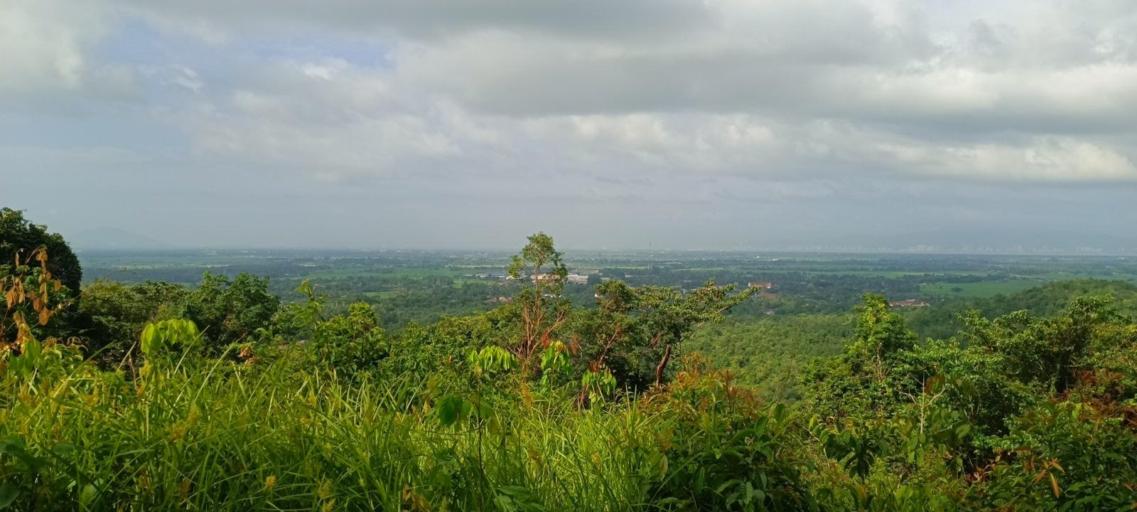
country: MY
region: Kedah
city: Sungai Petani
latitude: 5.6016
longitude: 100.4483
